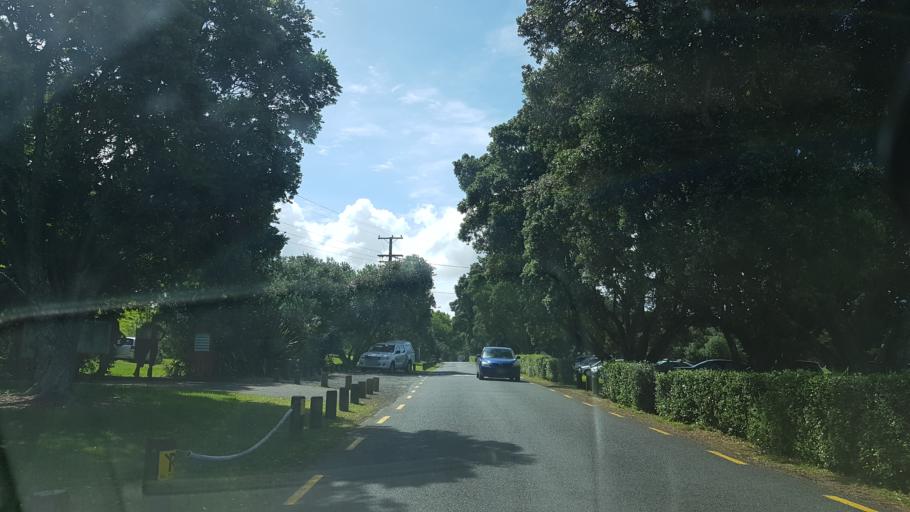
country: NZ
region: Auckland
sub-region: Auckland
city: Rothesay Bay
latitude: -36.6852
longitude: 174.7495
